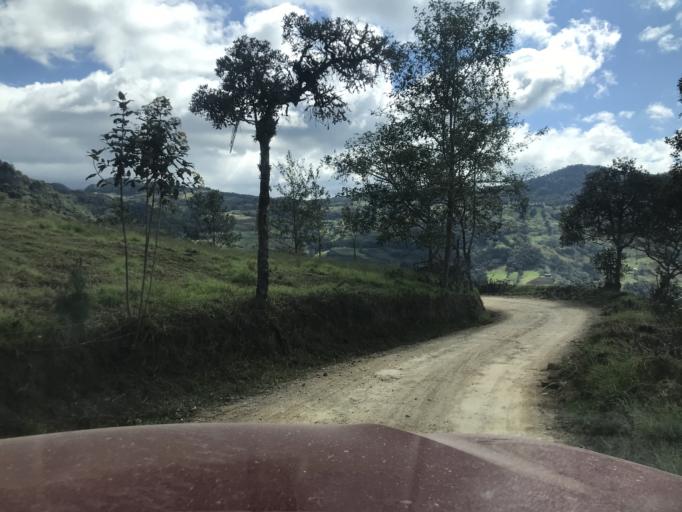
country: PE
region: Cajamarca
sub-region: Provincia de Chota
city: Querocoto
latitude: -6.3436
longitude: -79.0499
